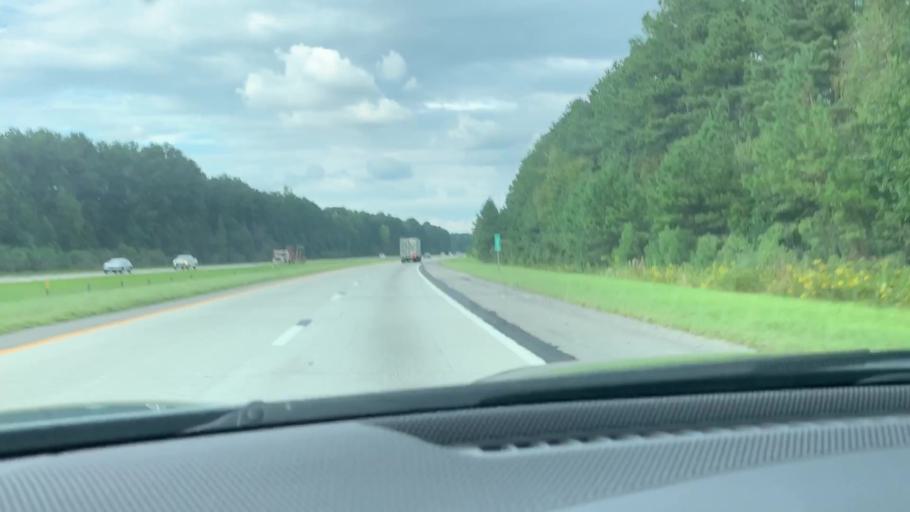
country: US
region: South Carolina
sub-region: Dorchester County
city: Saint George
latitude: 33.3090
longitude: -80.5538
